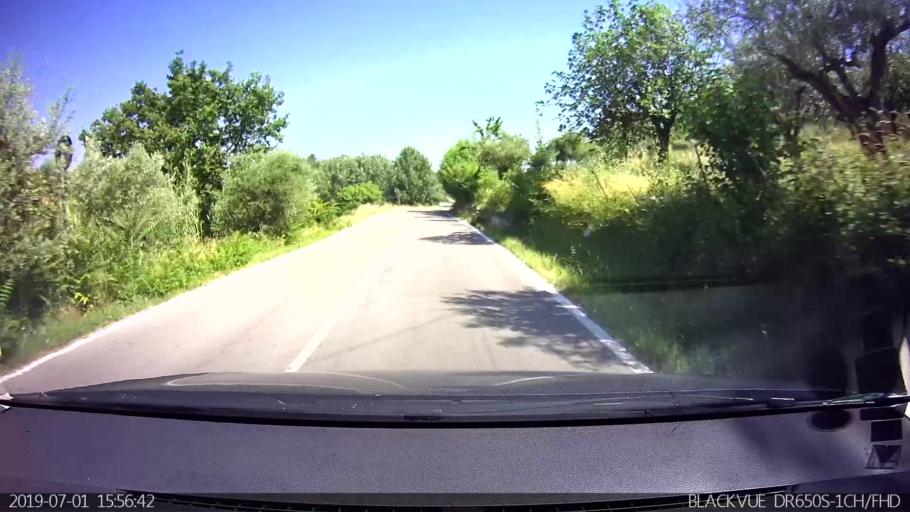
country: IT
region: Latium
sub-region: Provincia di Frosinone
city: Veroli
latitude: 41.6810
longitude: 13.4173
